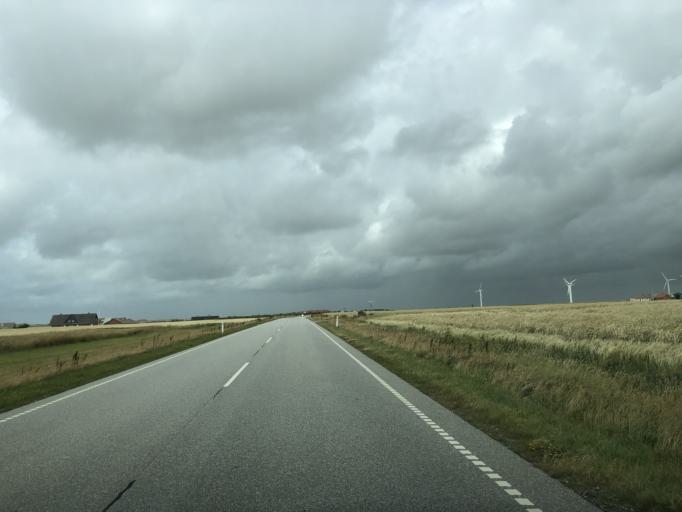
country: DK
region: Central Jutland
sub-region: Lemvig Kommune
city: Harboore
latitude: 56.4572
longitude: 8.1306
